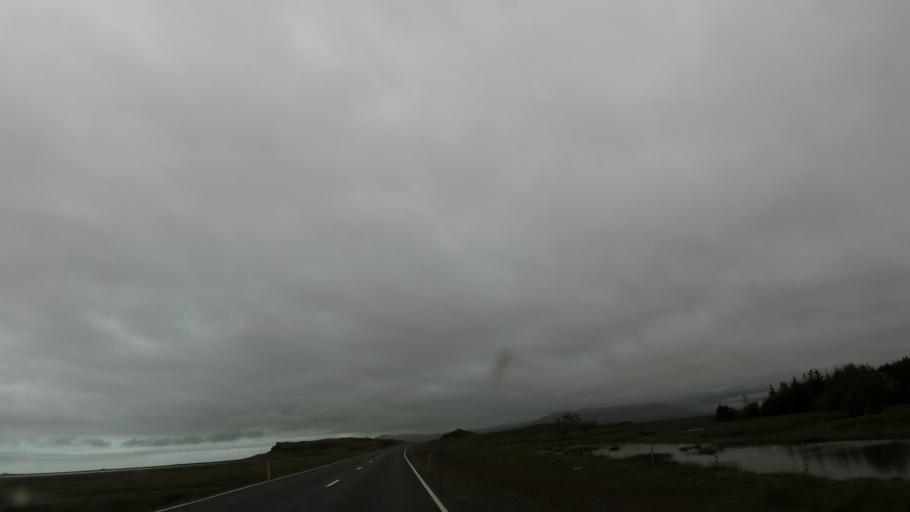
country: IS
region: East
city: Hoefn
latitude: 64.2677
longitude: -15.5036
